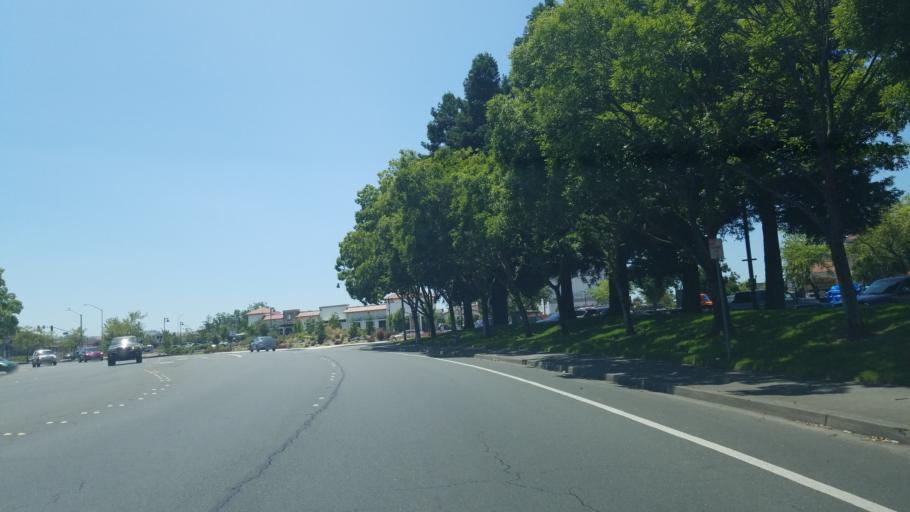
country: US
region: California
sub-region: Sonoma County
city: Rohnert Park
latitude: 38.3647
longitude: -122.7144
